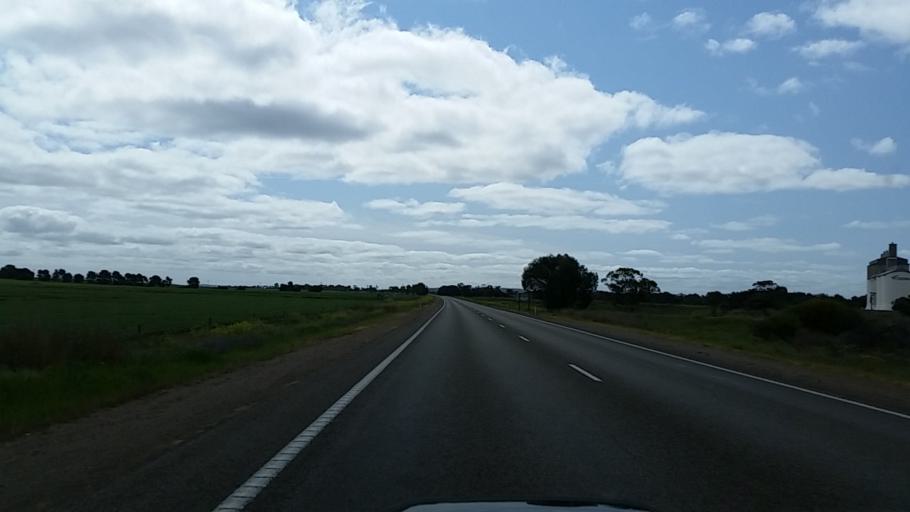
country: AU
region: South Australia
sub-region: Port Pirie City and Dists
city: Crystal Brook
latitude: -33.5507
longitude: 138.2205
